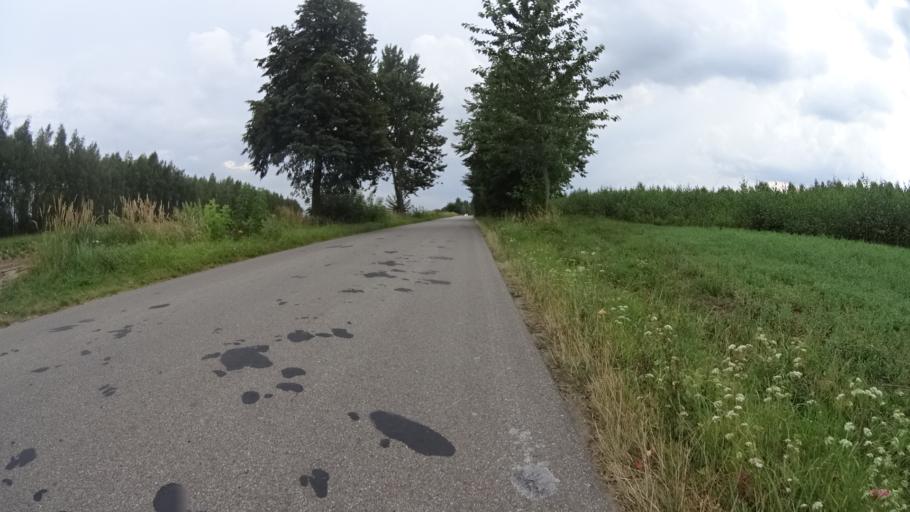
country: PL
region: Masovian Voivodeship
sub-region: Powiat grojecki
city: Goszczyn
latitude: 51.6833
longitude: 20.8610
